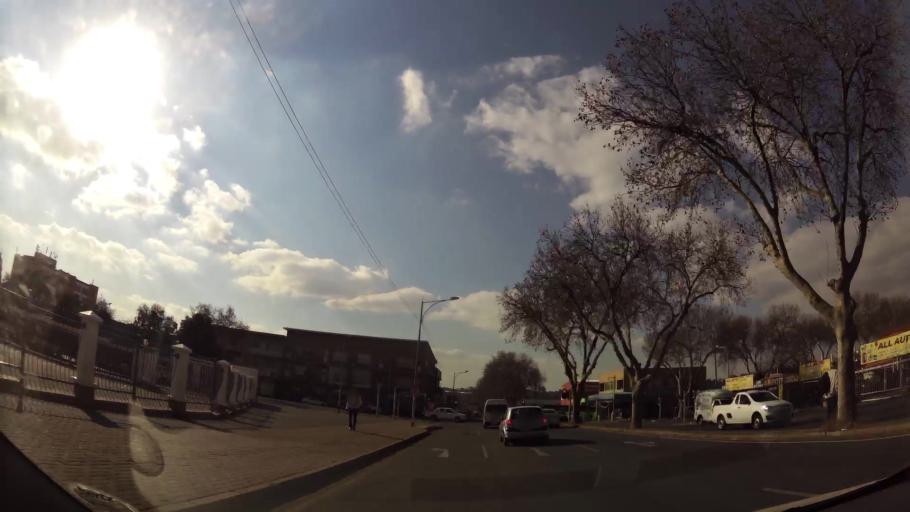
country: ZA
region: Gauteng
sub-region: West Rand District Municipality
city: Krugersdorp
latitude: -26.1002
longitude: 27.7739
